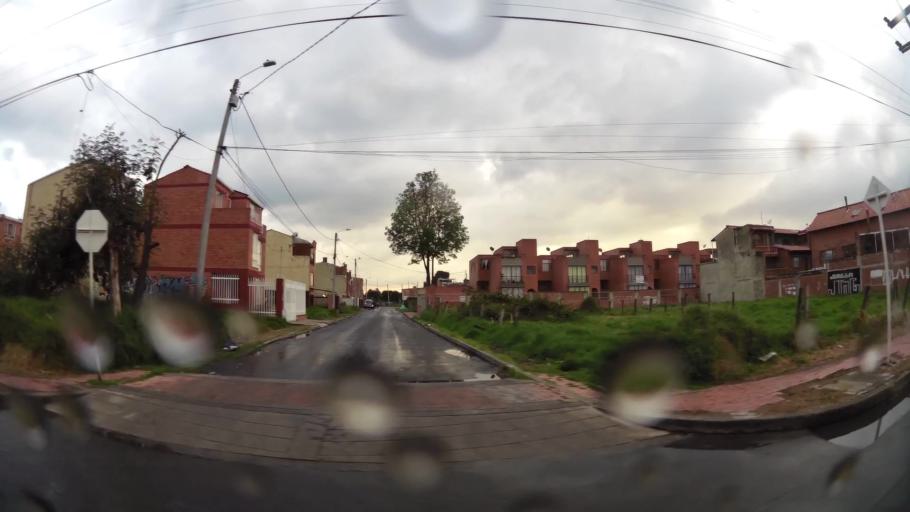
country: CO
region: Cundinamarca
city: Chia
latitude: 4.8690
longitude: -74.0559
